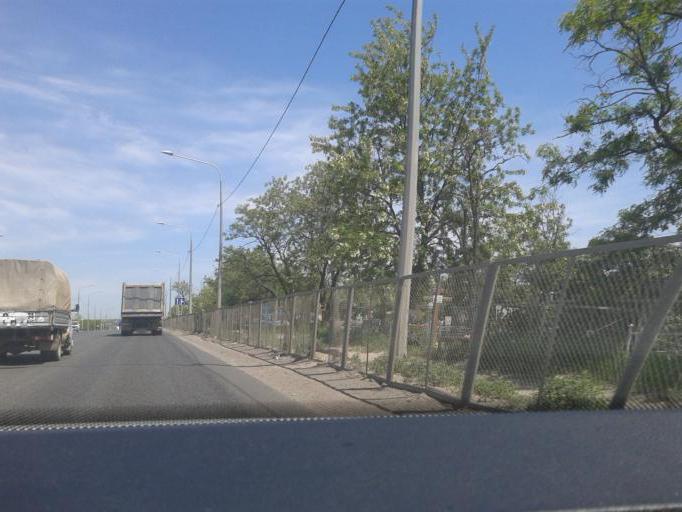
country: RU
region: Volgograd
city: Gorodishche
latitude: 48.7833
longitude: 44.5202
